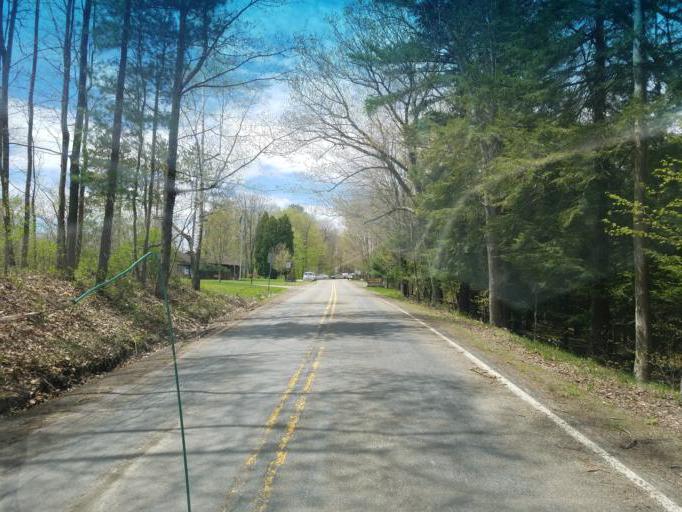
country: US
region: Pennsylvania
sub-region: Tioga County
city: Wellsboro
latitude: 41.6986
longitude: -77.4505
